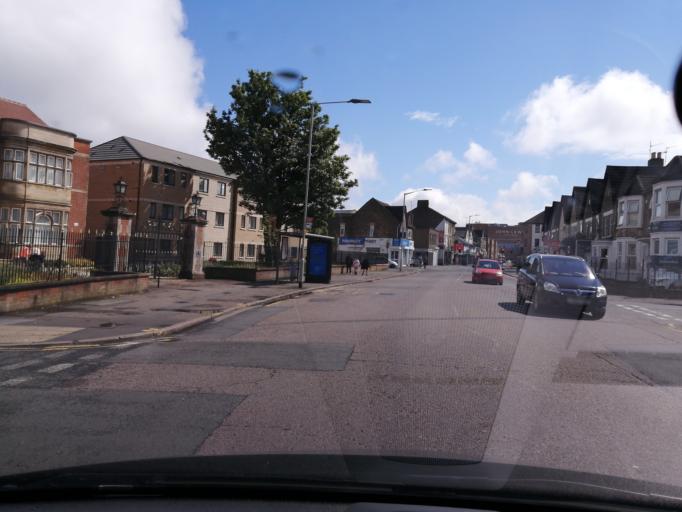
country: GB
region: England
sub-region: Peterborough
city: Peterborough
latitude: 52.5777
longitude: -0.2436
